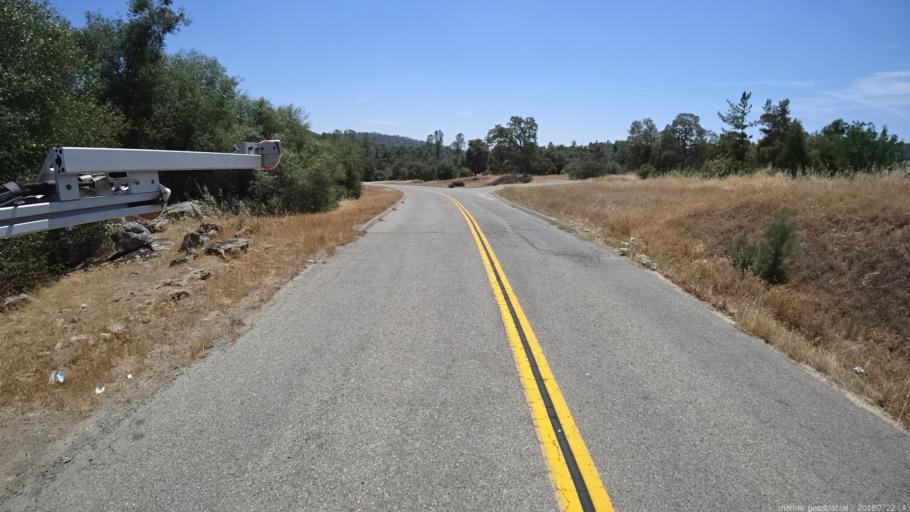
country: US
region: California
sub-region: Madera County
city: Yosemite Lakes
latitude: 37.2079
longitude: -119.7282
